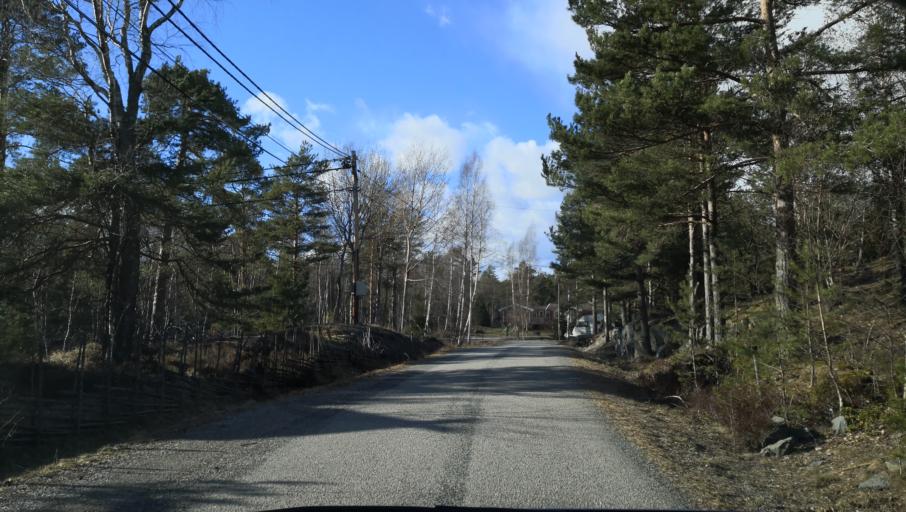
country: SE
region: Stockholm
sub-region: Varmdo Kommun
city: Hemmesta
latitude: 59.2452
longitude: 18.5156
